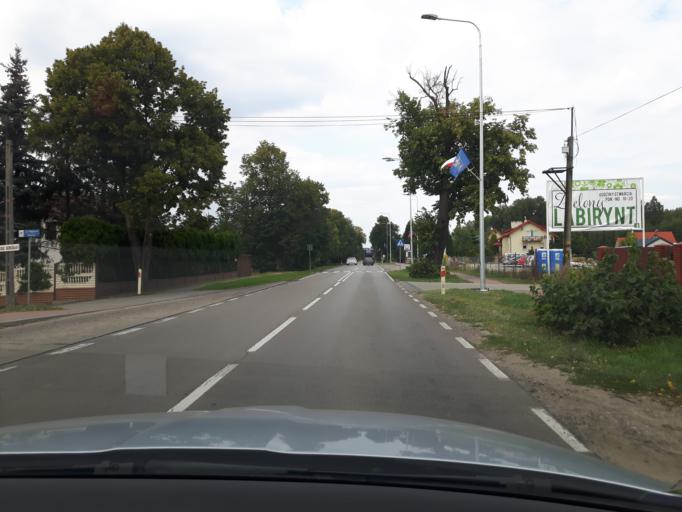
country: PL
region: Masovian Voivodeship
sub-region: Powiat legionowski
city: Nieporet
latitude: 52.4072
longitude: 21.0385
